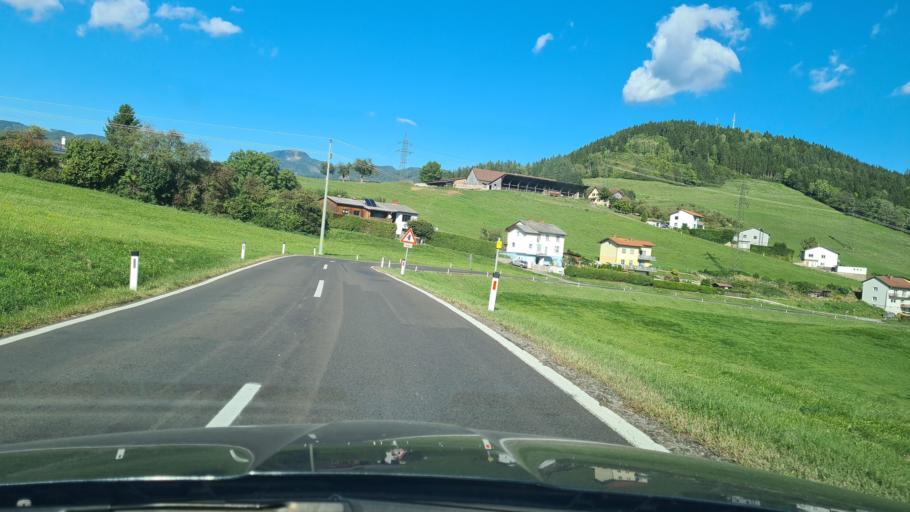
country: AT
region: Styria
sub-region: Politischer Bezirk Leoben
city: Trofaiach
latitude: 47.4036
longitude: 15.0057
